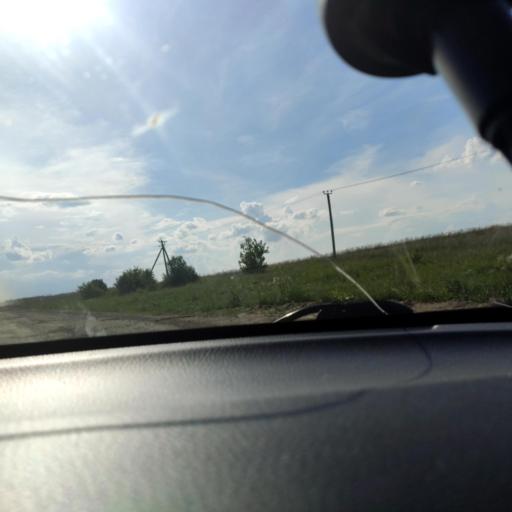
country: RU
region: Tatarstan
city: Verkhniy Uslon
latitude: 55.6485
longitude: 48.9372
